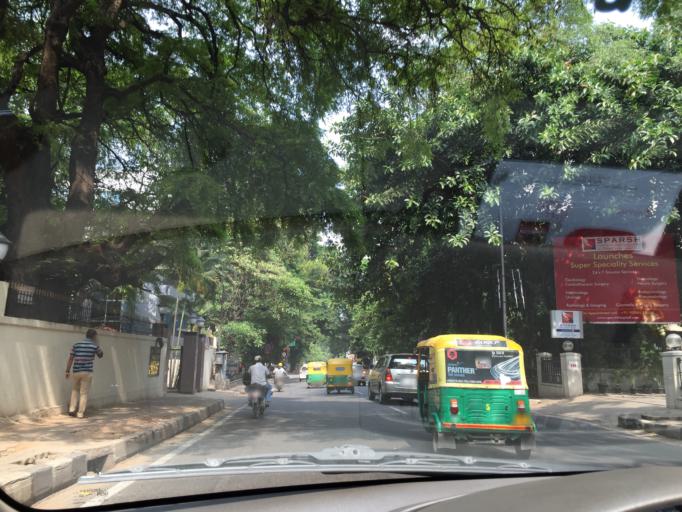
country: IN
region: Karnataka
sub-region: Bangalore Urban
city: Bangalore
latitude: 12.9835
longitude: 77.5948
